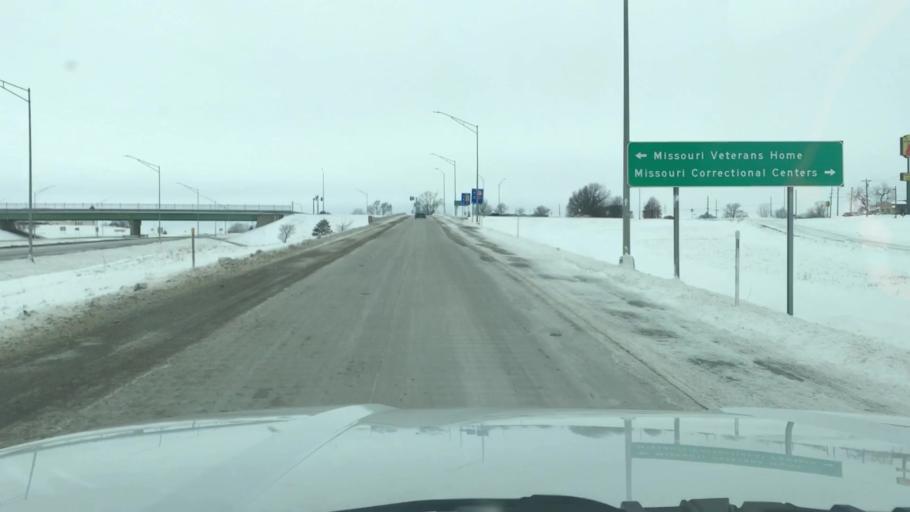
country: US
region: Missouri
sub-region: Clinton County
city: Cameron
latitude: 39.7546
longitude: -94.2312
